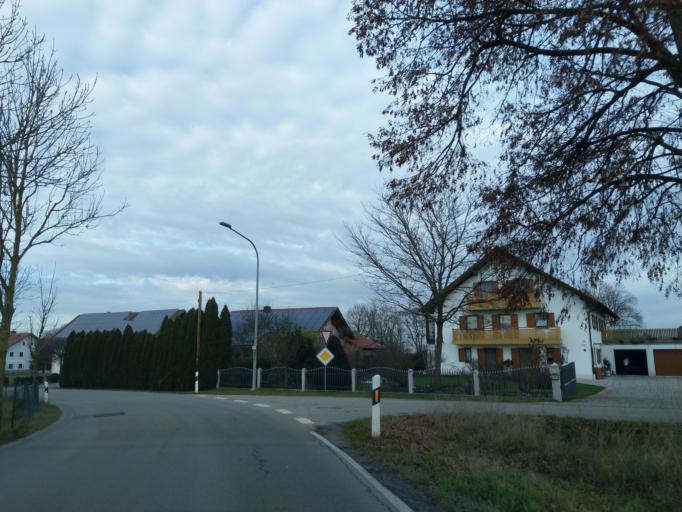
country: DE
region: Bavaria
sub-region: Lower Bavaria
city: Aholming
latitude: 48.7162
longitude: 12.9062
